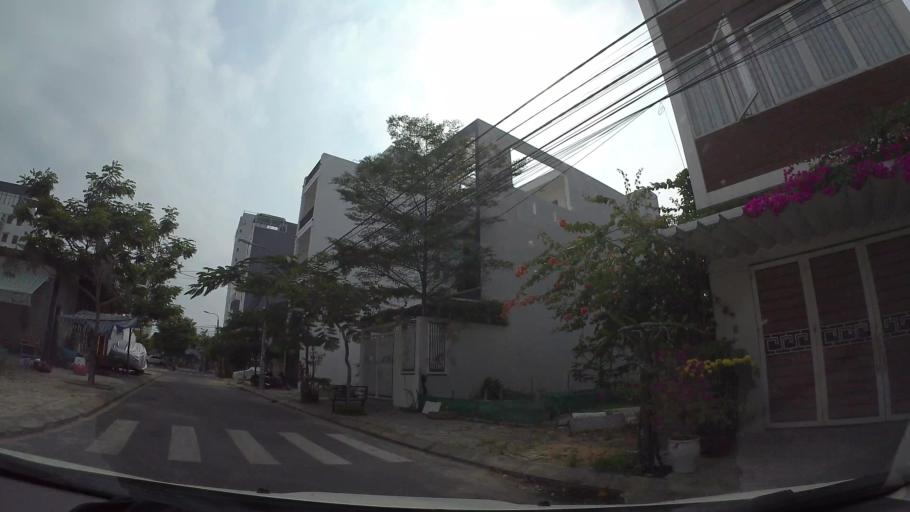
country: VN
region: Da Nang
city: Son Tra
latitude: 16.0722
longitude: 108.2374
